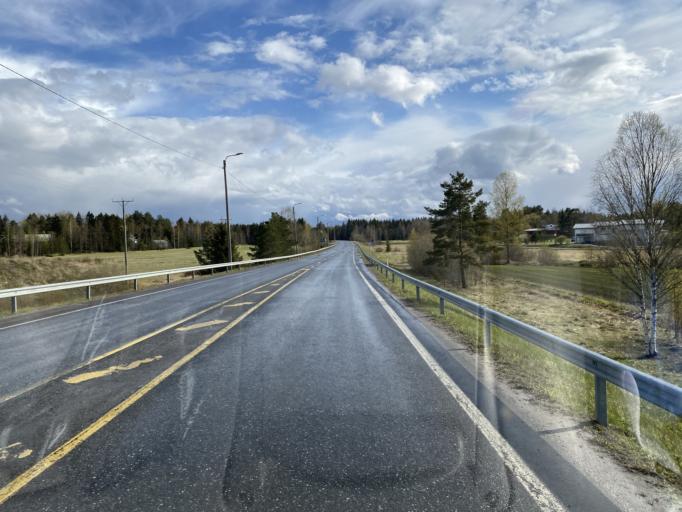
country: FI
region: Pirkanmaa
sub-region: Etelae-Pirkanmaa
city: Viiala
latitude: 61.2226
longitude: 23.7387
